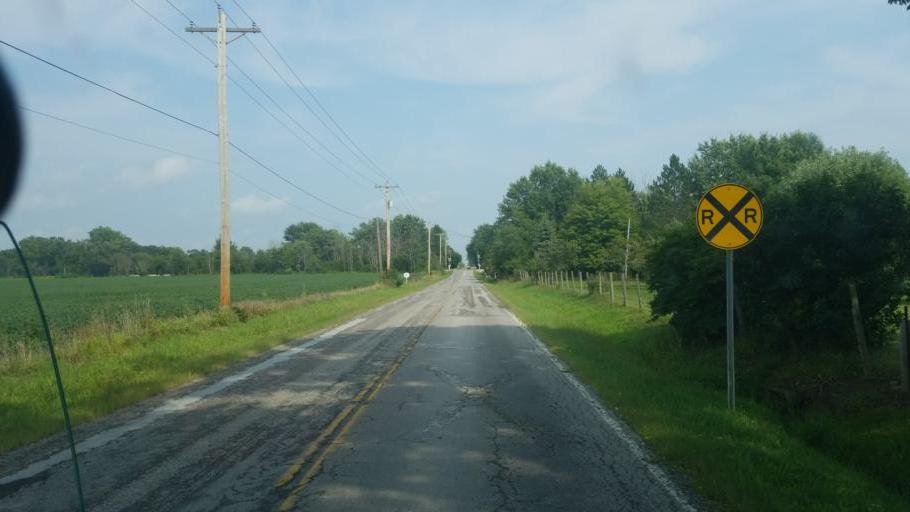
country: US
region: Ohio
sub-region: Medina County
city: Lodi
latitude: 41.1363
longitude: -82.0535
